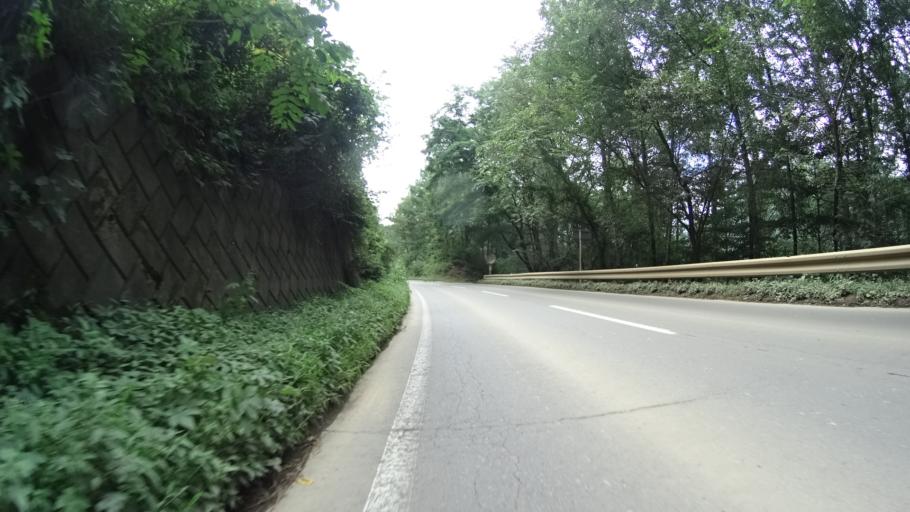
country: JP
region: Nagano
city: Saku
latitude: 35.9619
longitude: 138.5407
